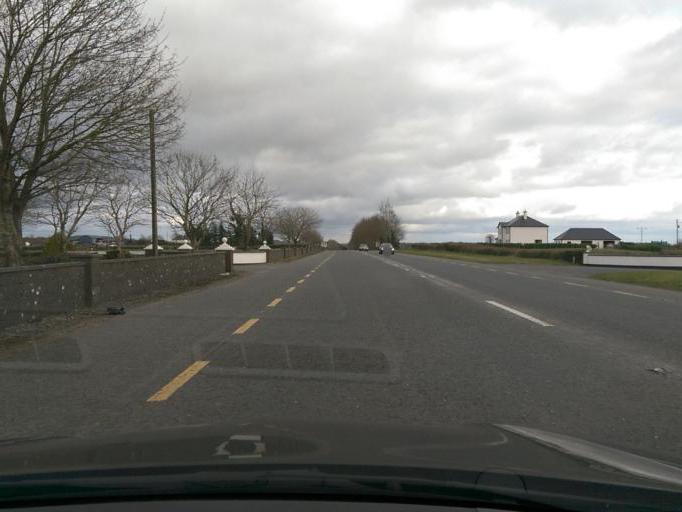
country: IE
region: Leinster
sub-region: An Iarmhi
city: Moate
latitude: 53.3937
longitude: -7.8301
